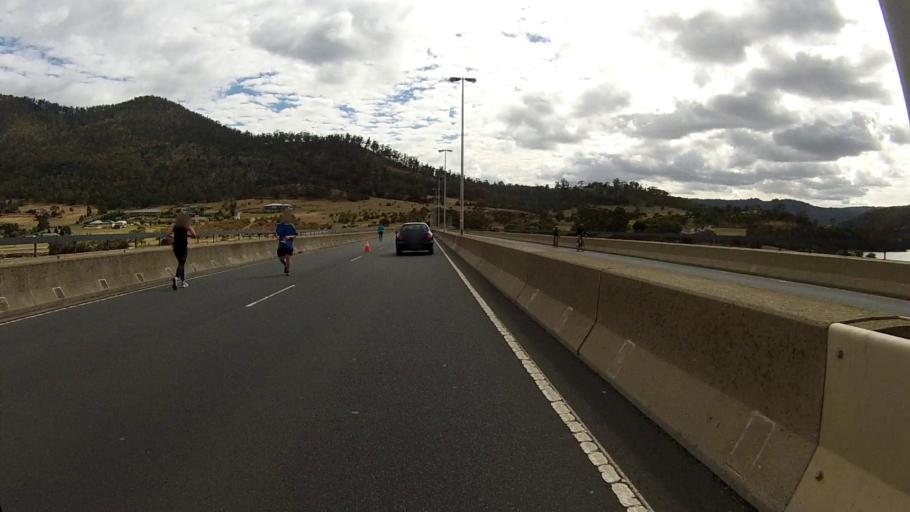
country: AU
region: Tasmania
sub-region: Glenorchy
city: Lutana
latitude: -42.8161
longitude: 147.3088
